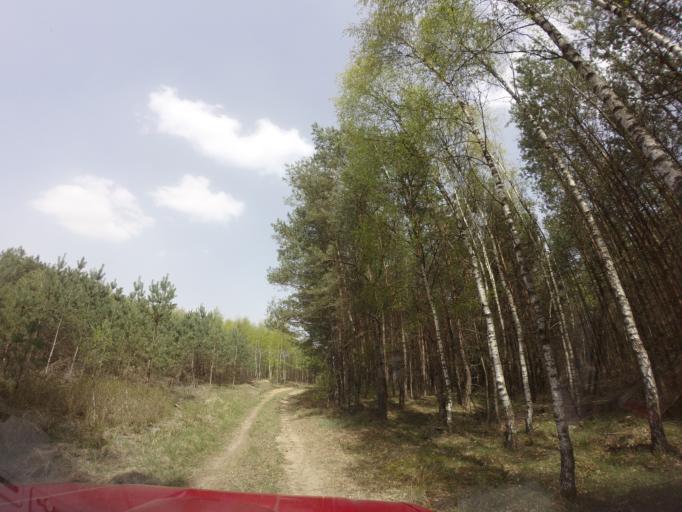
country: PL
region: West Pomeranian Voivodeship
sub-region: Powiat choszczenski
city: Drawno
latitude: 53.2718
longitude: 15.7084
